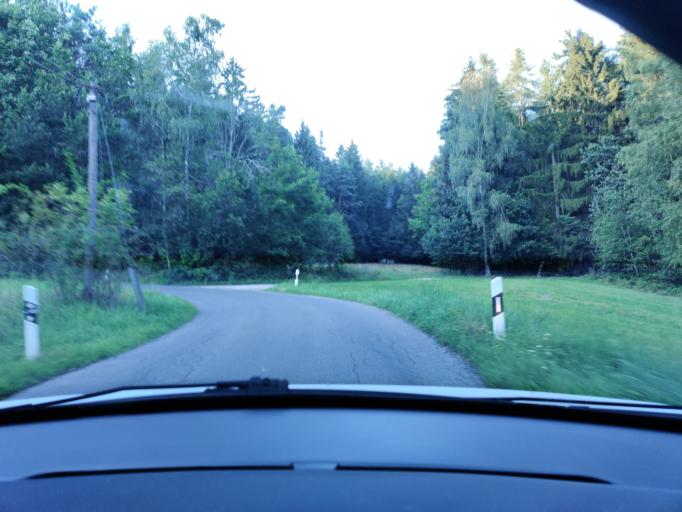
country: DE
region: Bavaria
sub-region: Upper Palatinate
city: Nabburg
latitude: 49.4174
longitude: 12.1778
